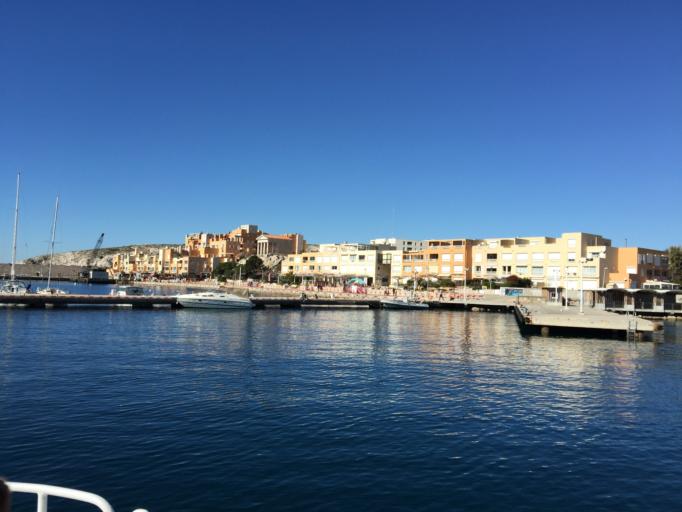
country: FR
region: Provence-Alpes-Cote d'Azur
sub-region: Departement des Bouches-du-Rhone
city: Marseille 07
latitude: 43.2786
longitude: 5.3071
